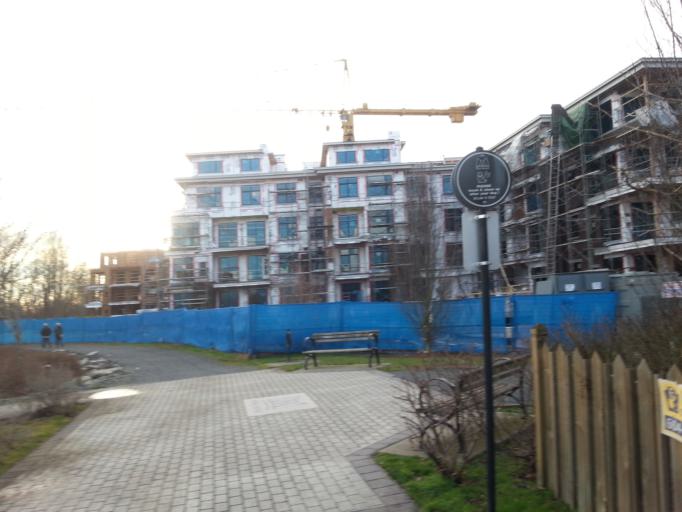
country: CA
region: British Columbia
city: New Westminster
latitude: 49.1916
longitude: -122.9255
